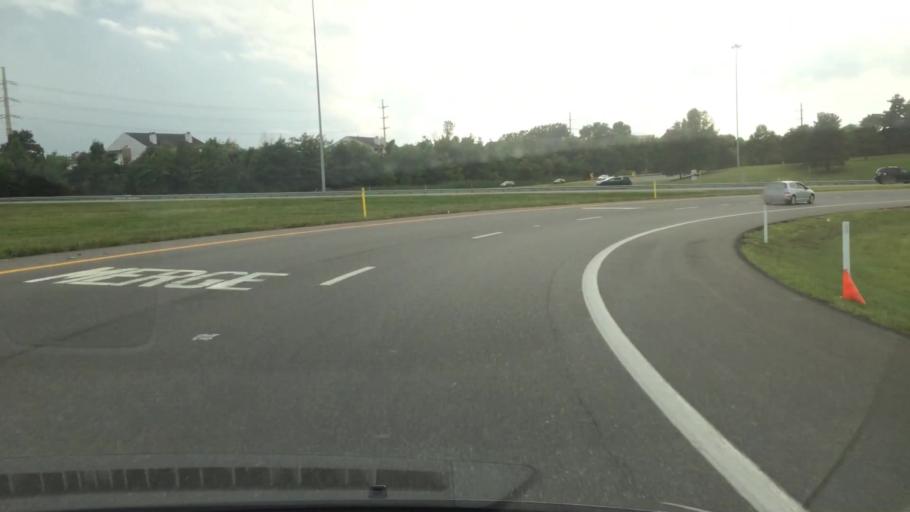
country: US
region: Ohio
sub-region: Cuyahoga County
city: Strongsville
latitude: 41.3118
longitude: -81.8094
